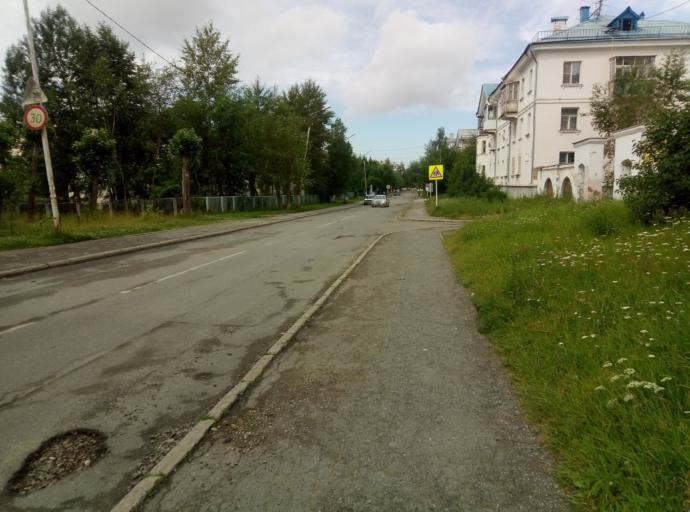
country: RU
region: Sverdlovsk
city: Krasnotur'insk
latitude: 59.7619
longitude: 60.2004
